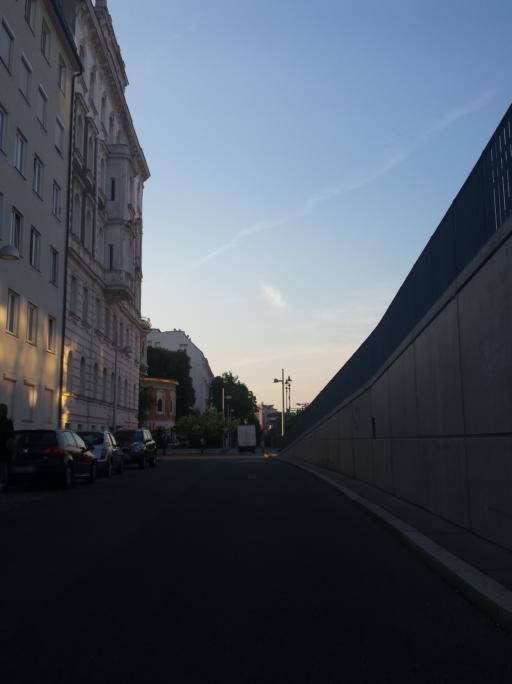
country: AT
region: Vienna
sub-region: Wien Stadt
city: Vienna
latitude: 48.1967
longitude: 16.3856
